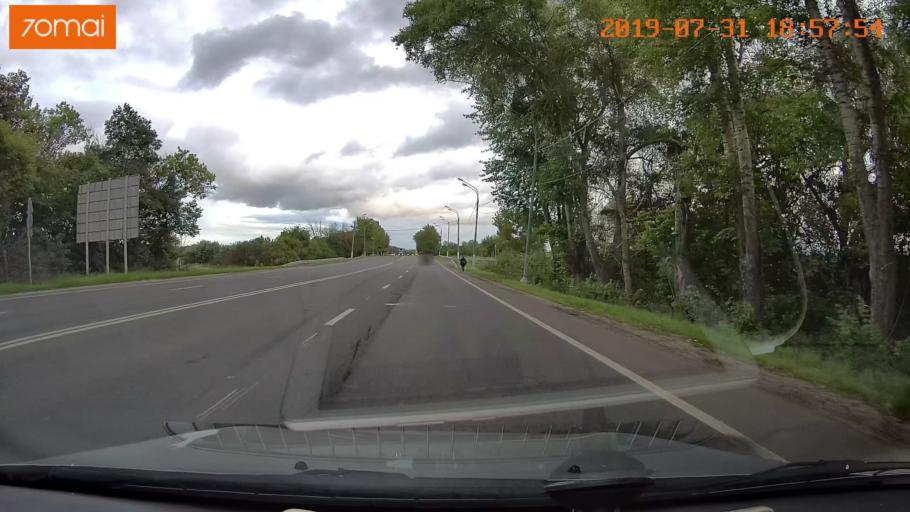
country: RU
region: Moskovskaya
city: Raduzhnyy
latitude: 55.1507
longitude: 38.6978
